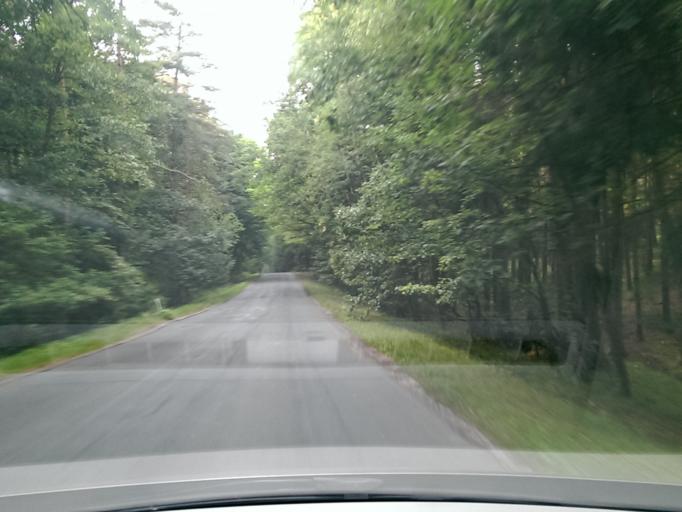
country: CZ
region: Central Bohemia
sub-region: Okres Mlada Boleslav
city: Zd'ar
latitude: 50.5196
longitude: 15.1090
